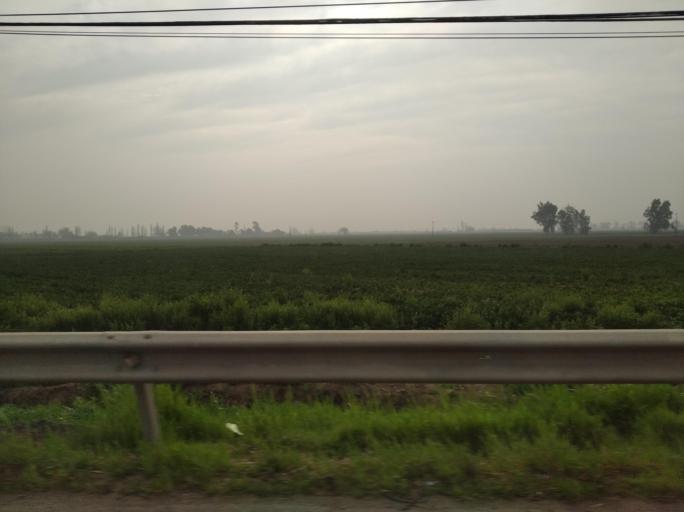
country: CL
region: Santiago Metropolitan
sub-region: Provincia de Chacabuco
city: Lampa
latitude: -33.3403
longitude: -70.8134
